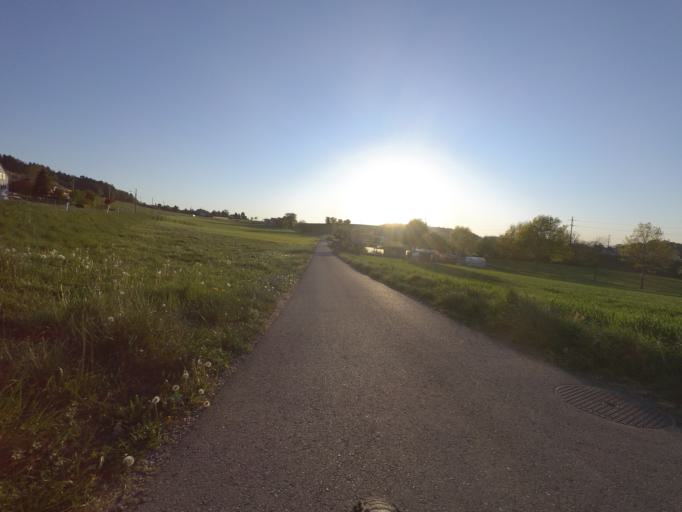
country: CH
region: Thurgau
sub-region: Frauenfeld District
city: Gachnang
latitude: 47.5428
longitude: 8.8359
